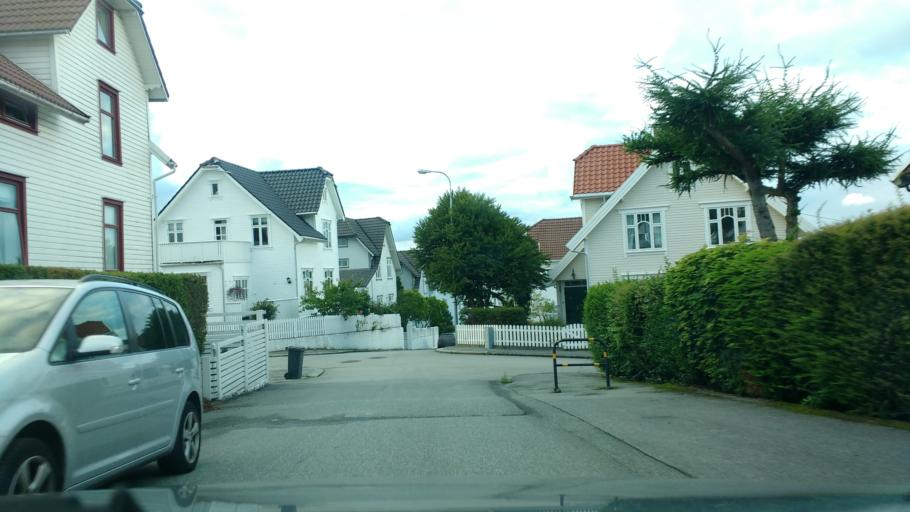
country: NO
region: Rogaland
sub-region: Stavanger
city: Stavanger
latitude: 58.9602
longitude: 5.7318
